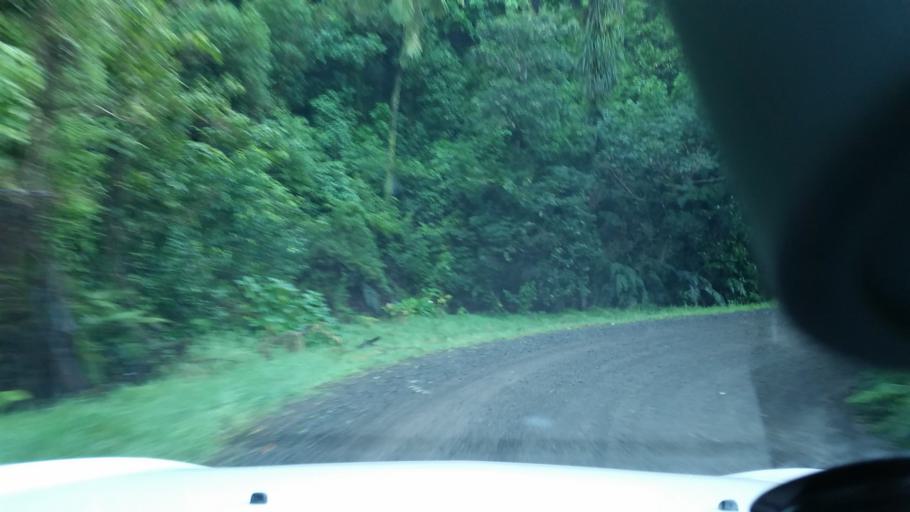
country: NZ
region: Bay of Plenty
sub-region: Kawerau District
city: Kawerau
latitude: -38.0285
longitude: 176.5575
